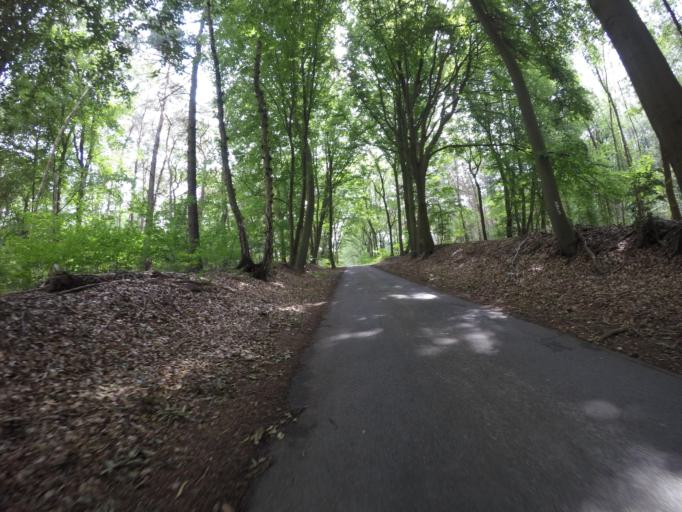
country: DE
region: North Rhine-Westphalia
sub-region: Regierungsbezirk Dusseldorf
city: Hamminkeln
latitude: 51.7333
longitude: 6.6598
